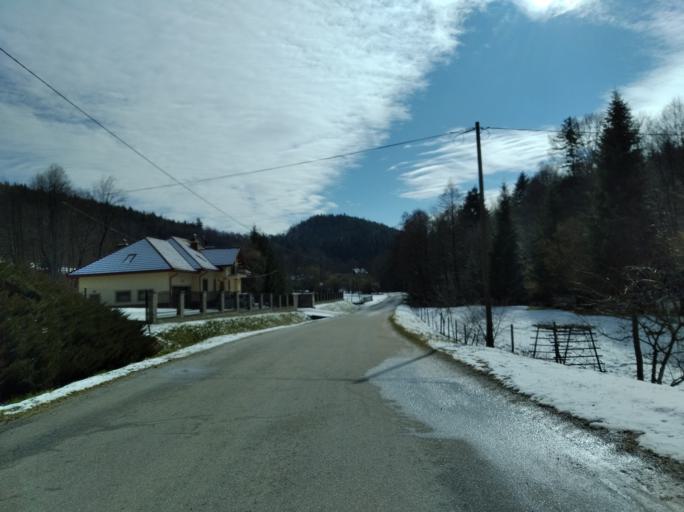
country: PL
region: Subcarpathian Voivodeship
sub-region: Powiat brzozowski
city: Jablonica Polska
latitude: 49.7454
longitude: 21.8829
